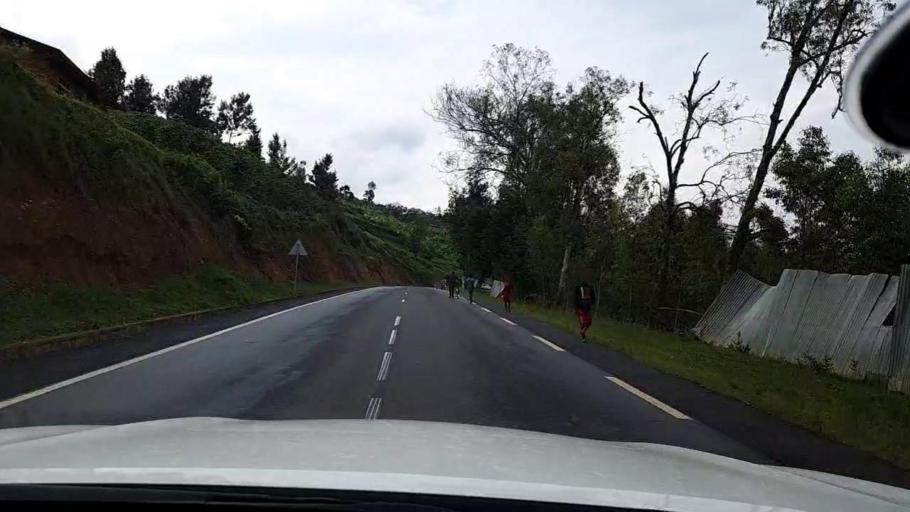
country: RW
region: Western Province
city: Kibuye
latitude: -2.1558
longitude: 29.2967
